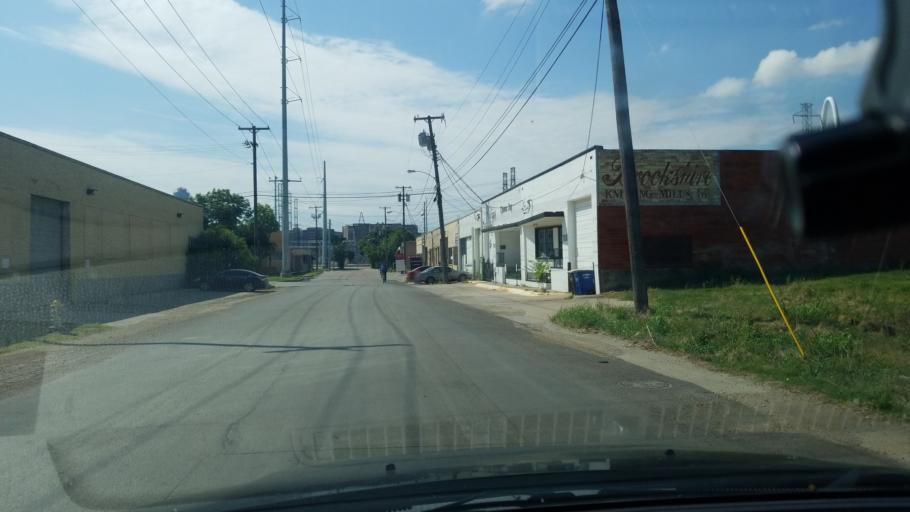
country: US
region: Texas
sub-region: Dallas County
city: Dallas
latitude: 32.7861
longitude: -96.8216
